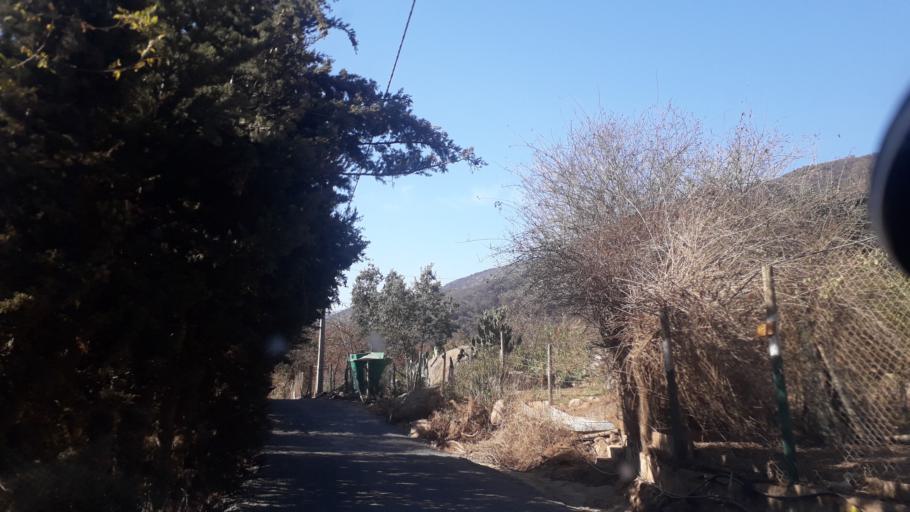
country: CL
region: Valparaiso
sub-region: Provincia de Marga Marga
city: Limache
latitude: -33.0814
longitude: -71.1002
